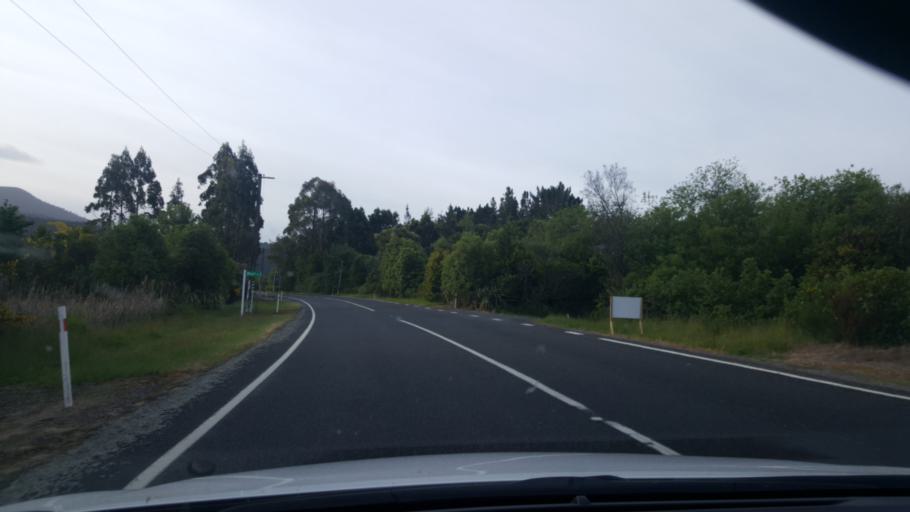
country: NZ
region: Waikato
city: Turangi
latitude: -38.9613
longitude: 175.7644
